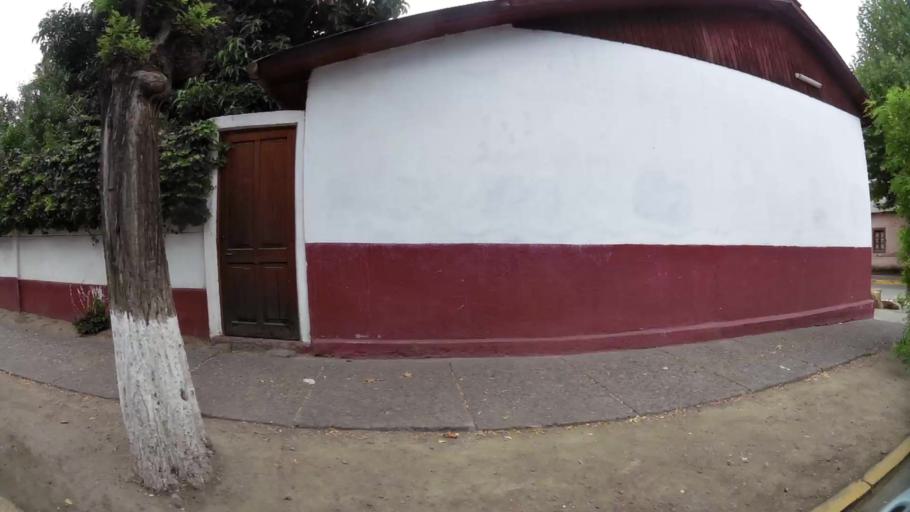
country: CL
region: O'Higgins
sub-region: Provincia de Cachapoal
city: Graneros
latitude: -34.0720
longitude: -70.7284
